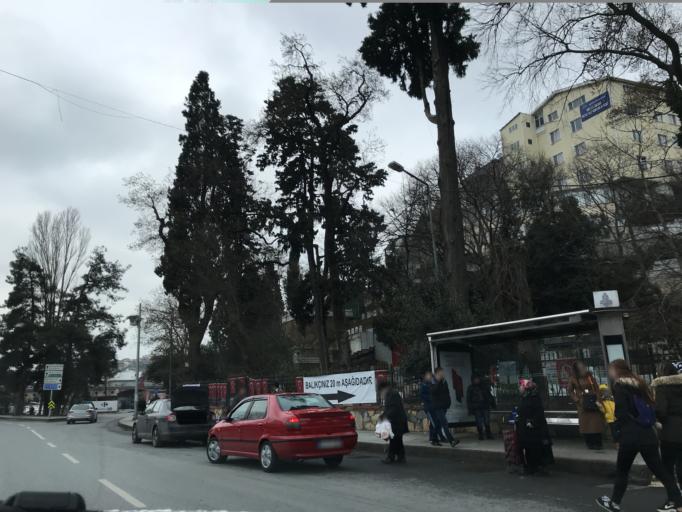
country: TR
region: Istanbul
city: Sisli
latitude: 41.1163
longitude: 29.0508
